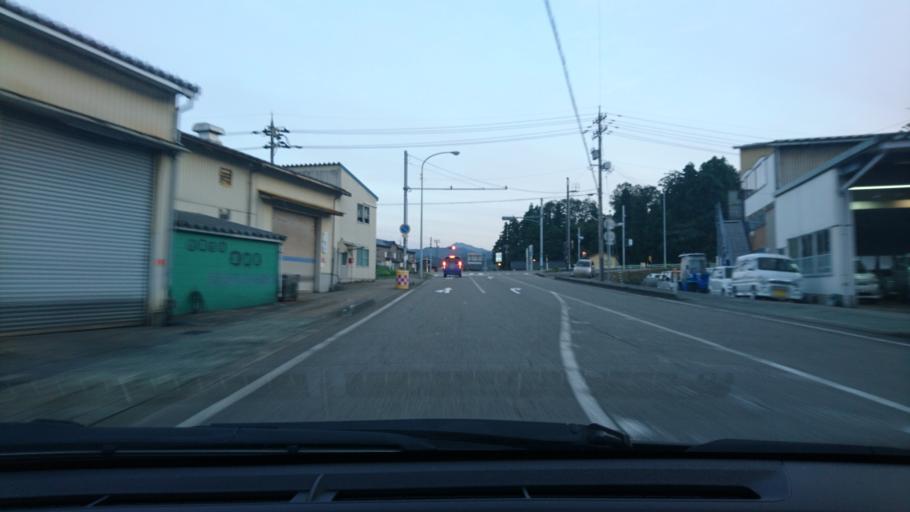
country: JP
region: Fukui
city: Maruoka
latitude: 36.2984
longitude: 136.3185
